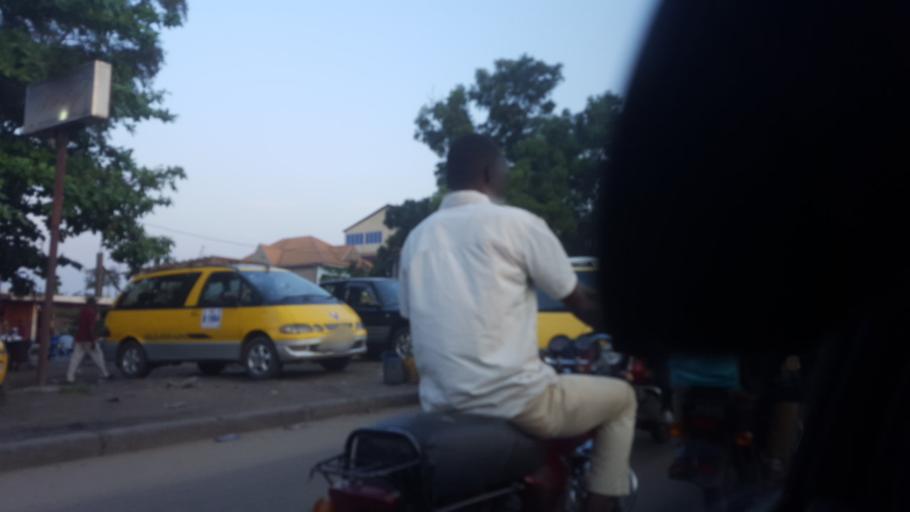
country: CD
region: Kinshasa
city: Kinshasa
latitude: -4.3484
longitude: 15.3249
